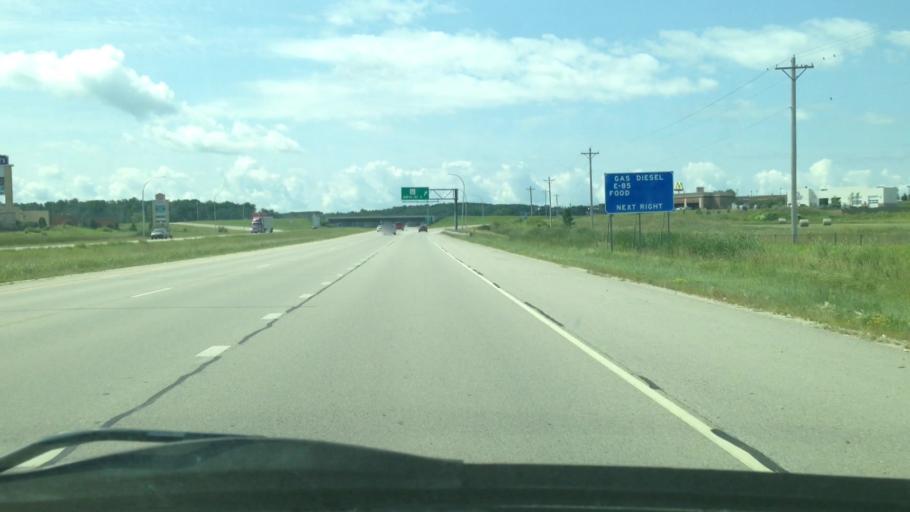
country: US
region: Minnesota
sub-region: Olmsted County
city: Rochester
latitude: 43.9586
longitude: -92.4660
